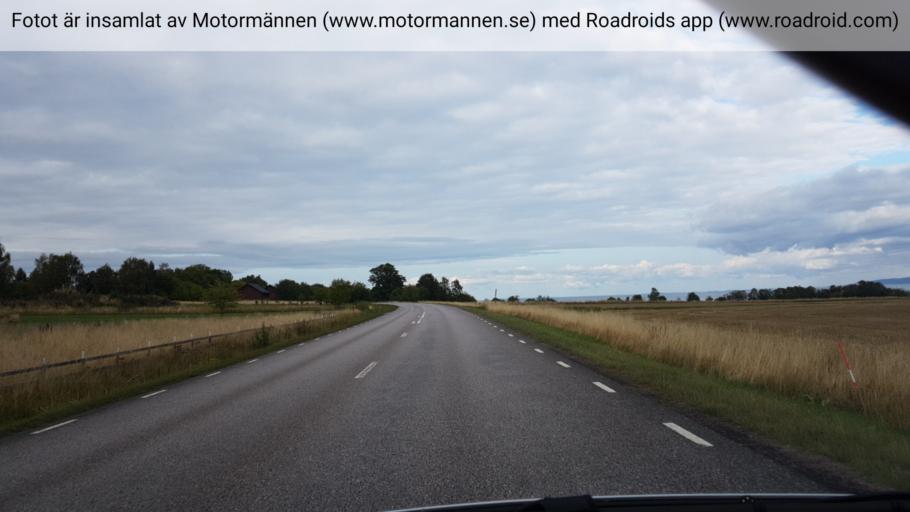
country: SE
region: Vaestra Goetaland
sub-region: Hjo Kommun
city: Hjo
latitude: 58.3291
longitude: 14.3295
